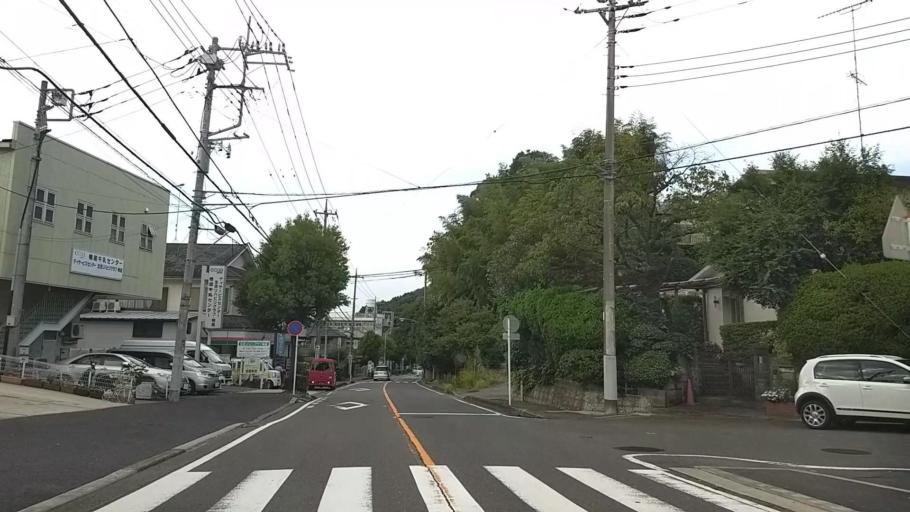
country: JP
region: Kanagawa
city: Yokohama
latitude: 35.4995
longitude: 139.5656
